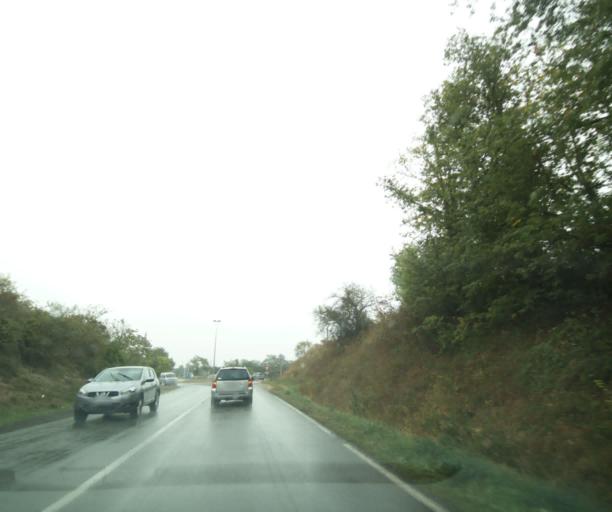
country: FR
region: Auvergne
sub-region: Departement du Puy-de-Dome
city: Cebazat
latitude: 45.8424
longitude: 3.1122
